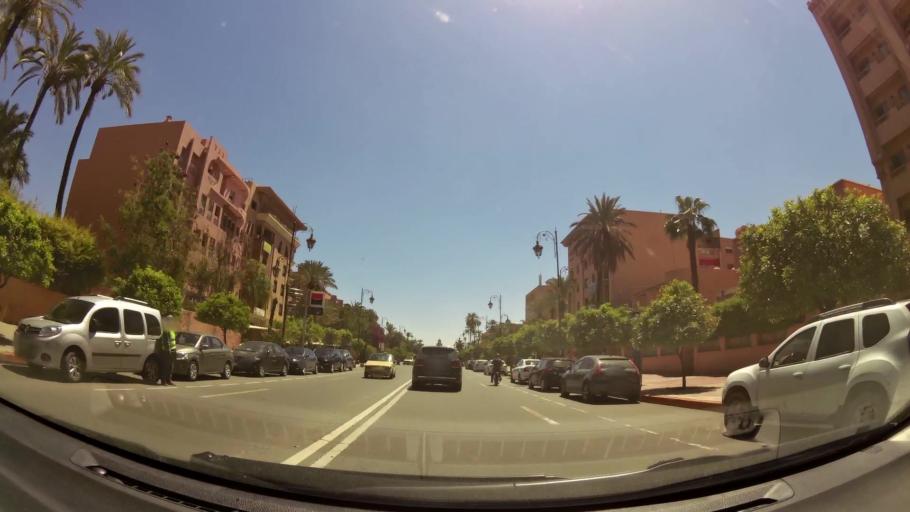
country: MA
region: Marrakech-Tensift-Al Haouz
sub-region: Marrakech
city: Marrakesh
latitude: 31.6308
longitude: -8.0052
